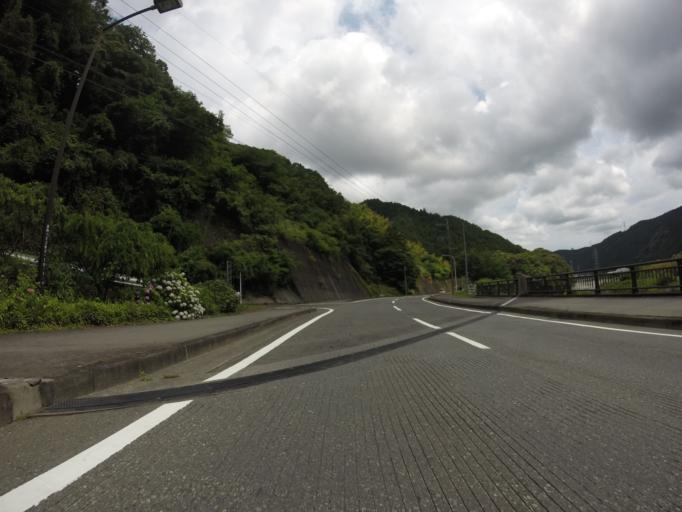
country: JP
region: Shizuoka
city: Shizuoka-shi
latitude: 35.0044
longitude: 138.2856
